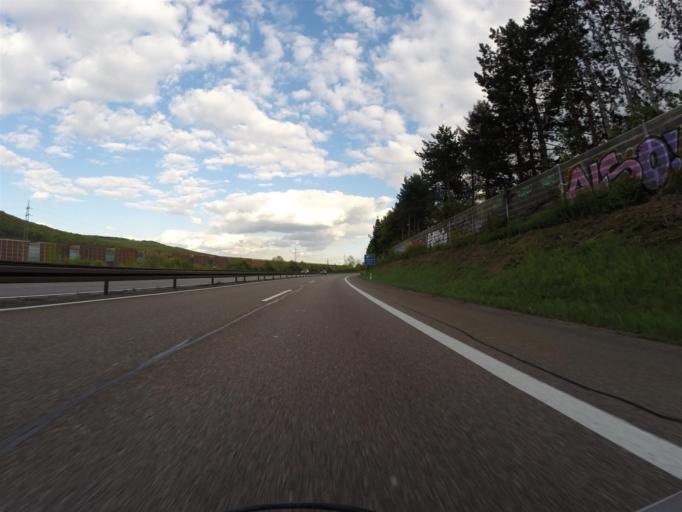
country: DE
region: Saarland
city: Bous
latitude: 49.2655
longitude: 6.8250
